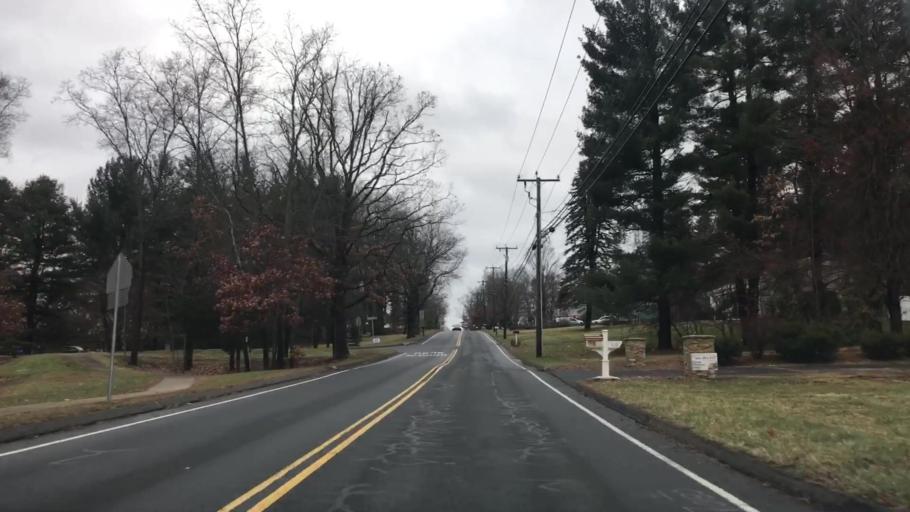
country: US
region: Connecticut
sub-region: Hartford County
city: Manchester
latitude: 41.8404
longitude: -72.5118
